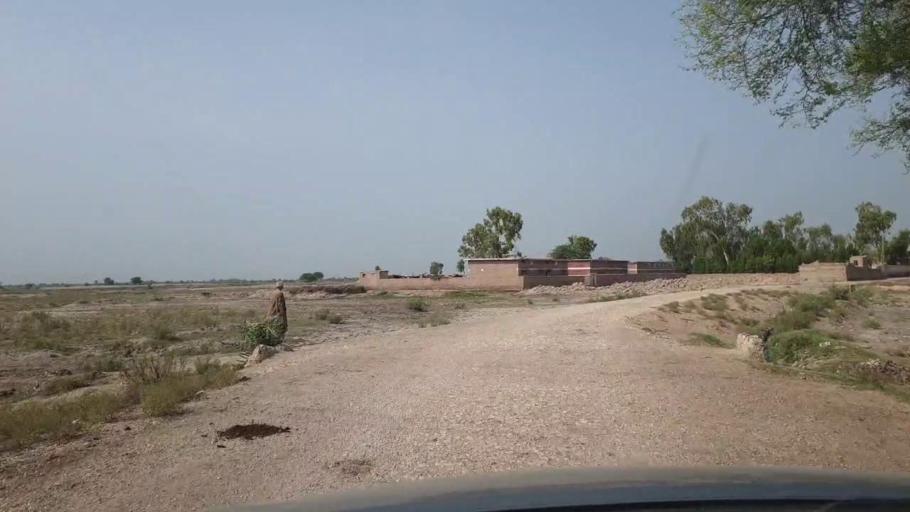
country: PK
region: Sindh
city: Lakhi
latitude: 27.8268
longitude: 68.6962
